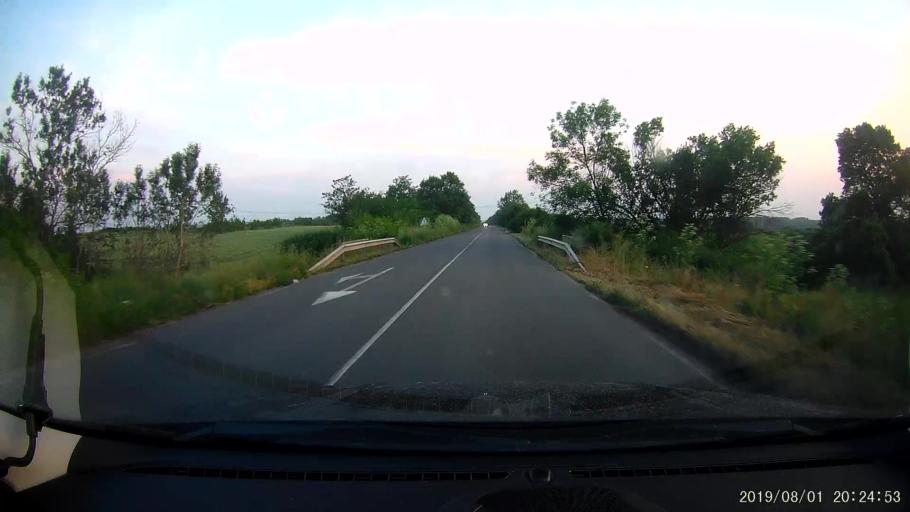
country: BG
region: Yambol
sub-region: Obshtina Elkhovo
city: Elkhovo
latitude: 42.2247
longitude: 26.5909
